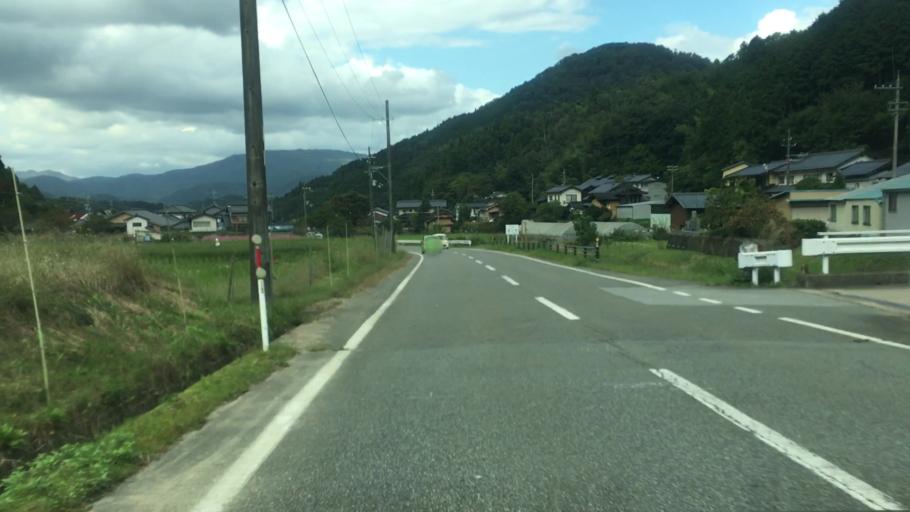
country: JP
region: Hyogo
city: Toyooka
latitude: 35.4342
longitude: 134.7352
